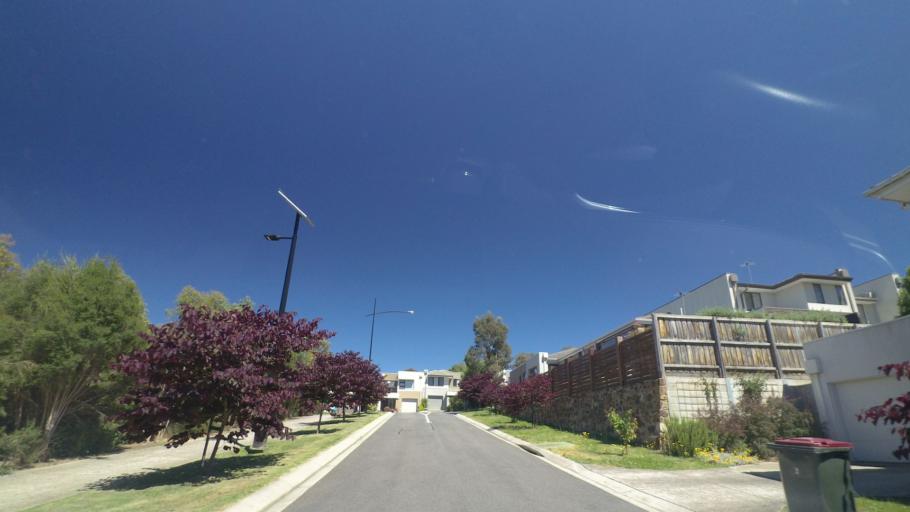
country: AU
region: Victoria
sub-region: Maroondah
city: Croydon North
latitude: -37.7800
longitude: 145.3012
